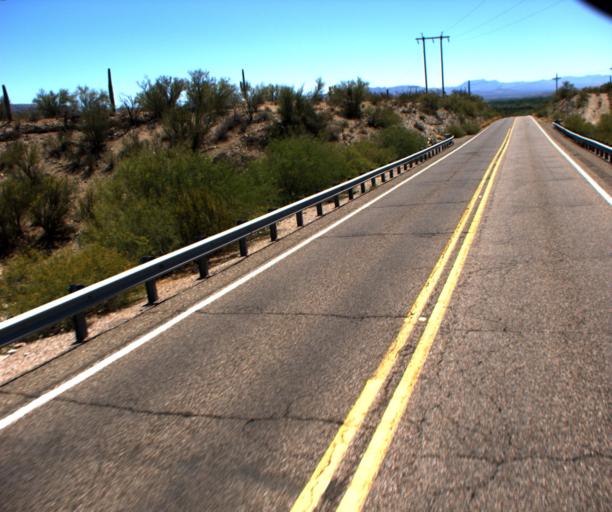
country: US
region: Arizona
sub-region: Pinal County
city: Kearny
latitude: 33.0188
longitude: -110.8478
